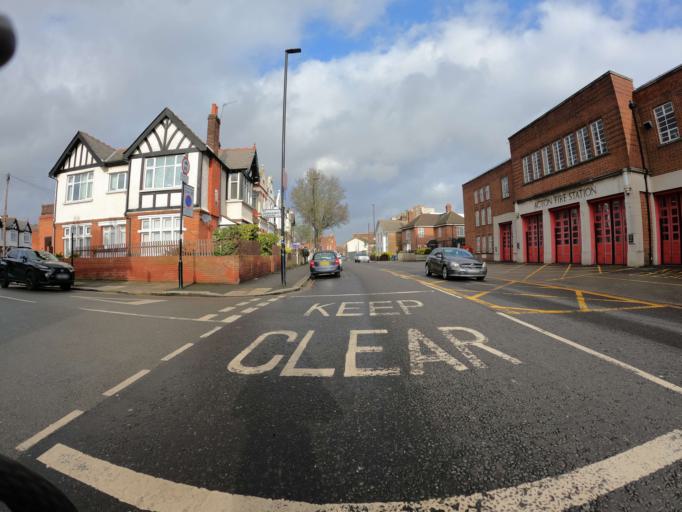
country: GB
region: England
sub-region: Greater London
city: Acton
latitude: 51.5070
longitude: -0.2775
